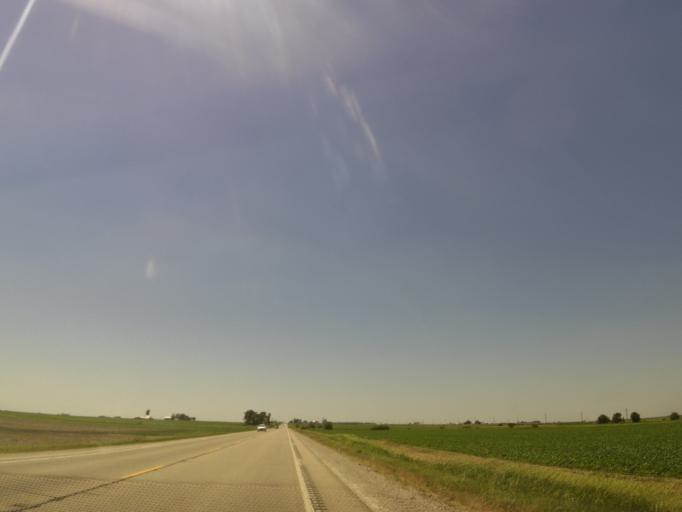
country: US
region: Illinois
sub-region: McLean County
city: Chenoa
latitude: 40.7412
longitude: -88.7490
